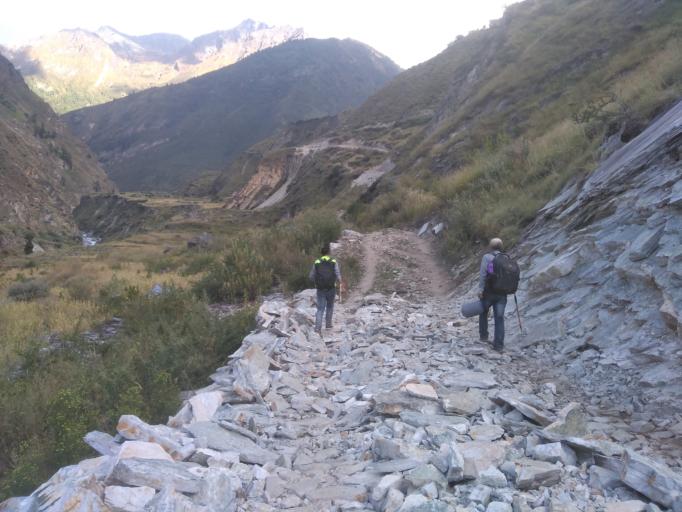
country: NP
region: Western Region
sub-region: Dhawalagiri Zone
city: Jomsom
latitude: 28.8835
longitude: 82.9872
